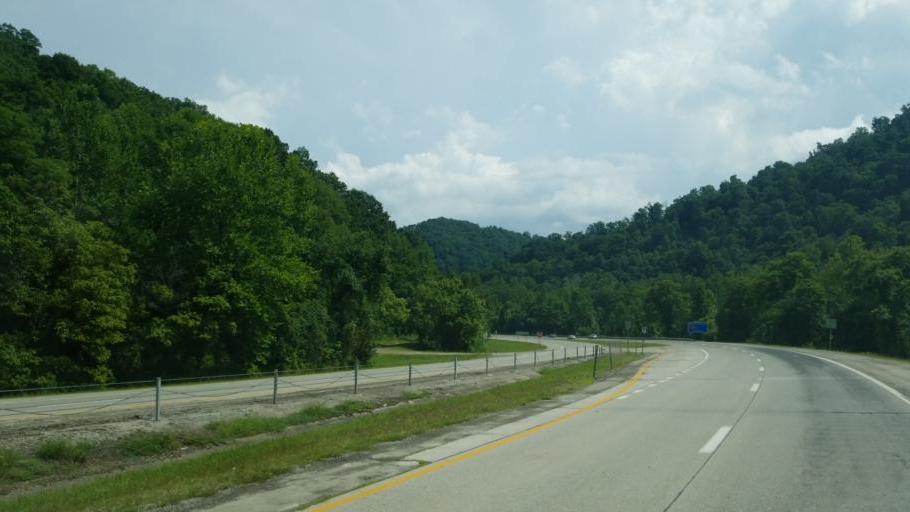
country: US
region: West Virginia
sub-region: Boone County
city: Madison
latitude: 38.1435
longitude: -81.8457
